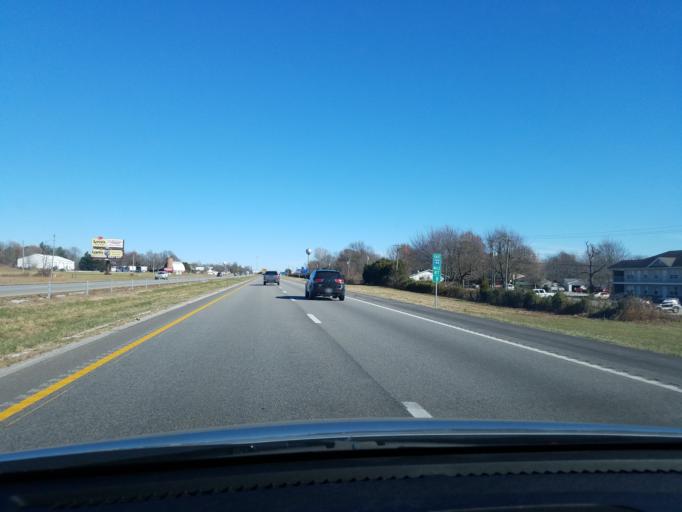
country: US
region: Missouri
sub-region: Greene County
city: Strafford
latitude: 37.2676
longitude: -93.1335
